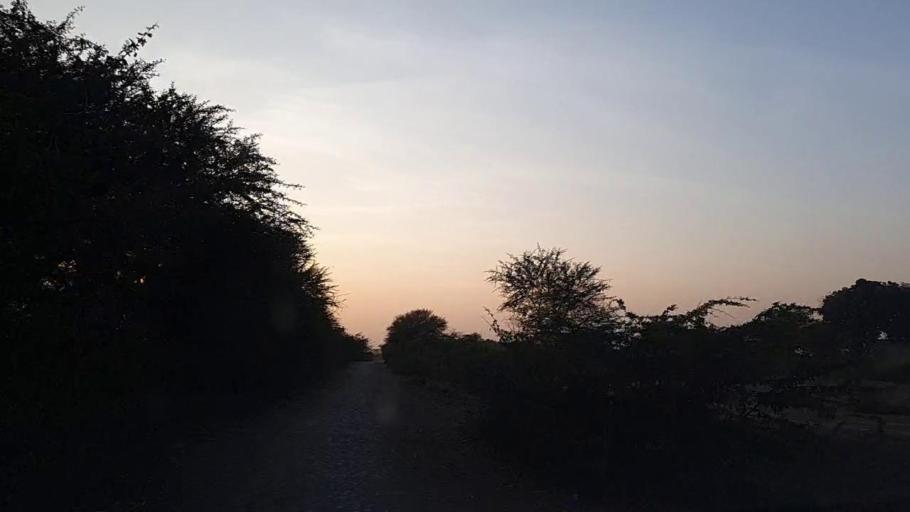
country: PK
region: Sindh
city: Naukot
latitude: 24.9531
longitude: 69.4271
